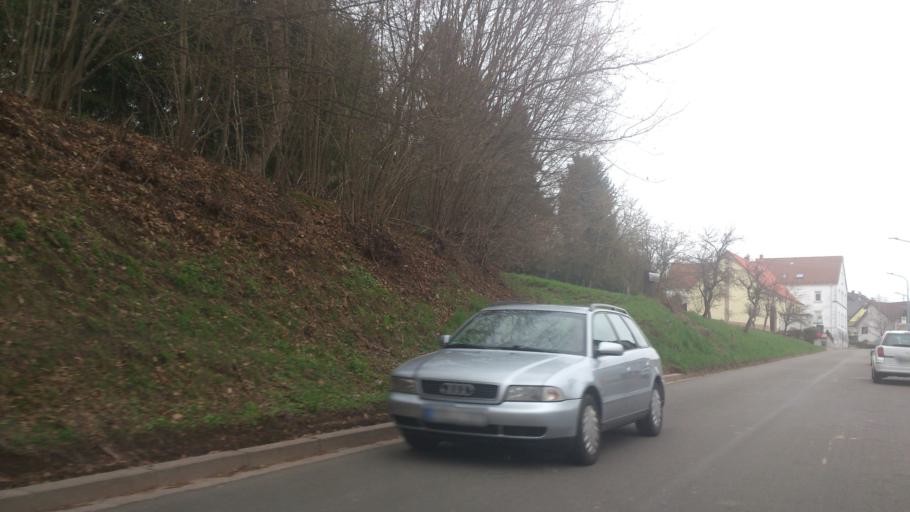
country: DE
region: Rheinland-Pfalz
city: Borsborn
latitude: 49.4392
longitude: 7.3971
